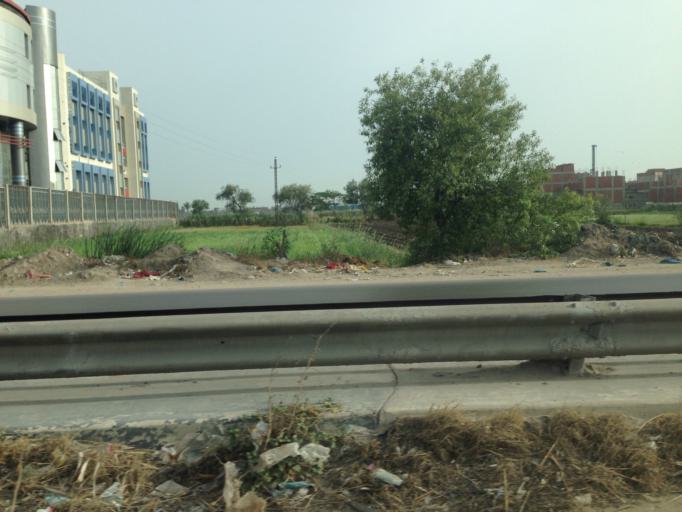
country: EG
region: Alexandria
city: Alexandria
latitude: 31.2028
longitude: 30.0162
